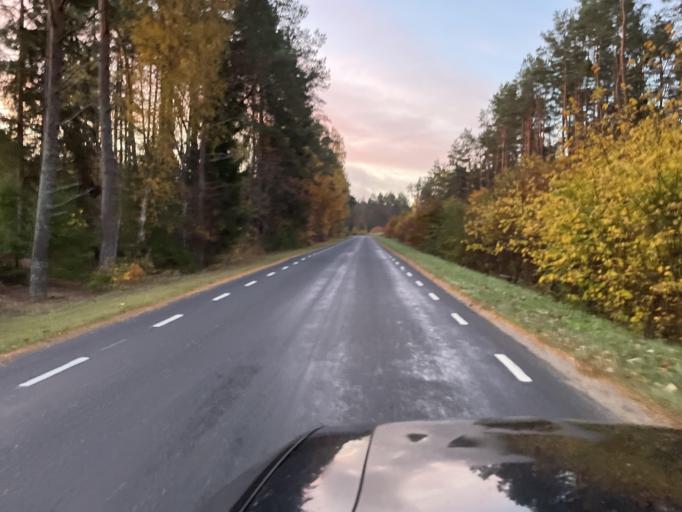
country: EE
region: Harju
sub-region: Nissi vald
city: Riisipere
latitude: 59.2537
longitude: 24.2302
